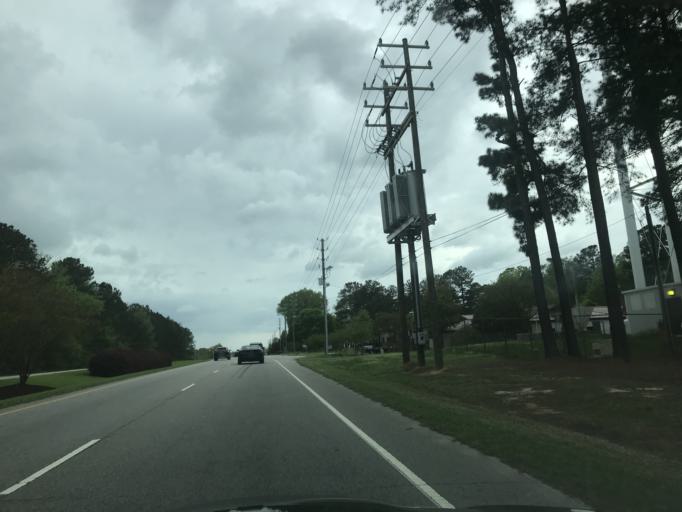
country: US
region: North Carolina
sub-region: Wake County
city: Knightdale
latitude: 35.7990
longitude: -78.4789
